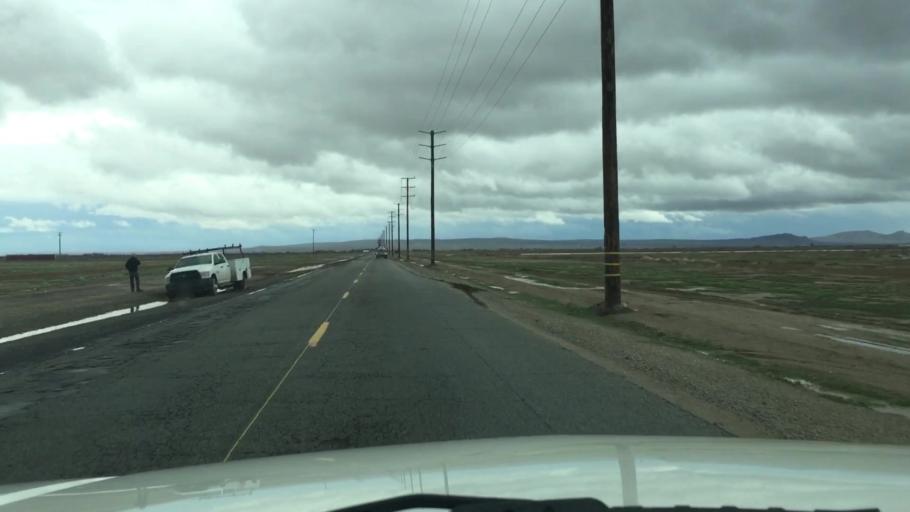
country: US
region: California
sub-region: Los Angeles County
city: Lancaster
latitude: 34.7635
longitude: -118.0002
